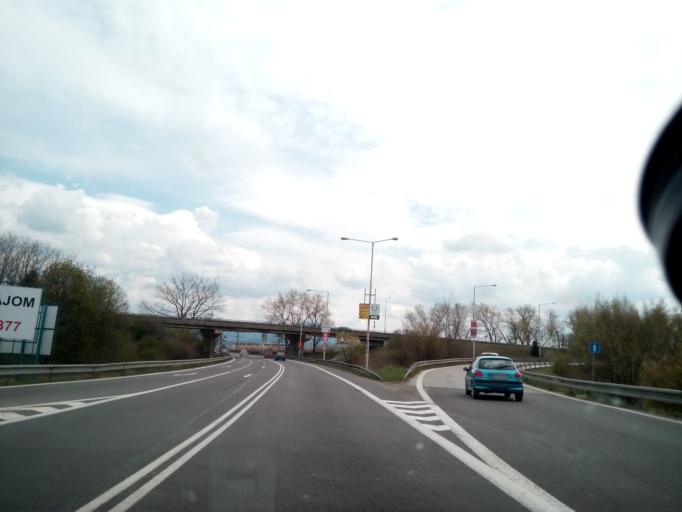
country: SK
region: Zilinsky
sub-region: Okres Zilina
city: Vrutky
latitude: 49.0949
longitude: 18.9233
